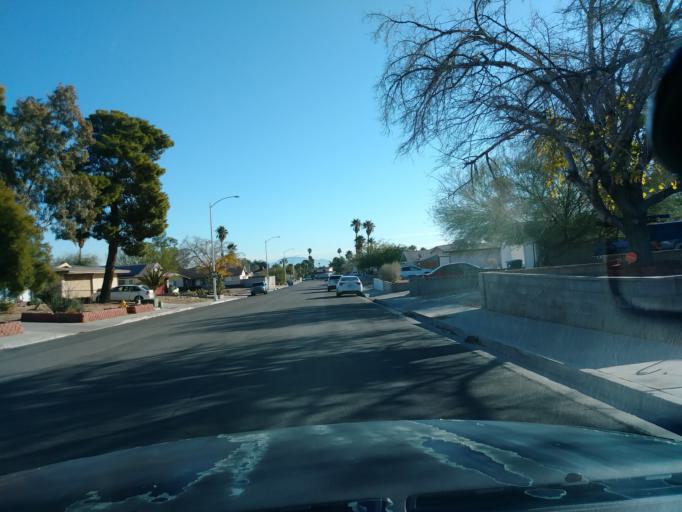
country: US
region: Nevada
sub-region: Clark County
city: Spring Valley
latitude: 36.1672
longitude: -115.2503
